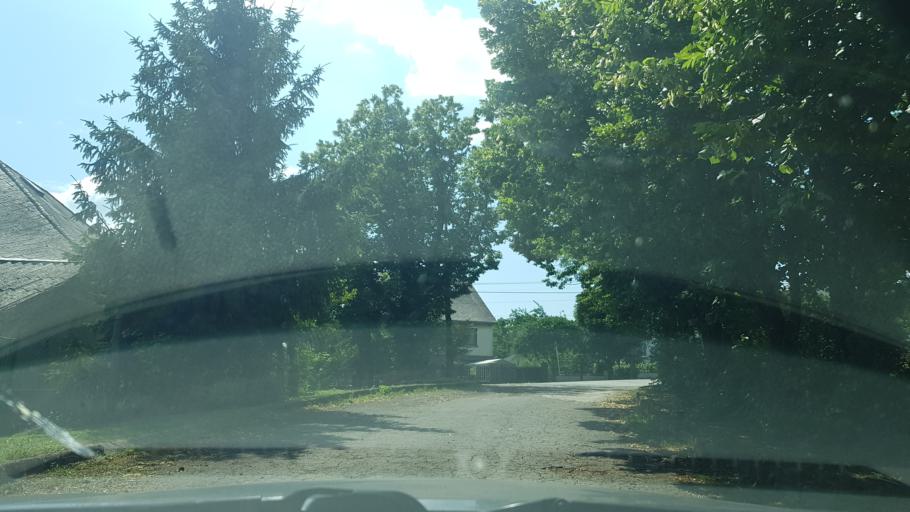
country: HU
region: Borsod-Abauj-Zemplen
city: Gonc
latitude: 48.5360
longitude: 21.4581
